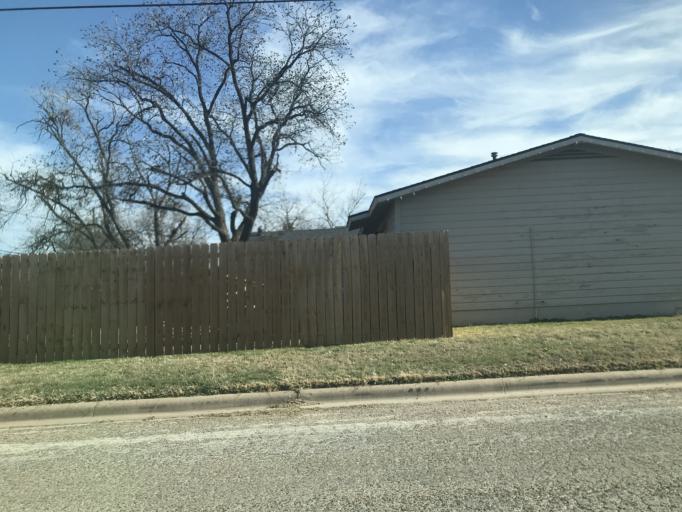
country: US
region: Texas
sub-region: Taylor County
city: Abilene
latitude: 32.4224
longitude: -99.7557
